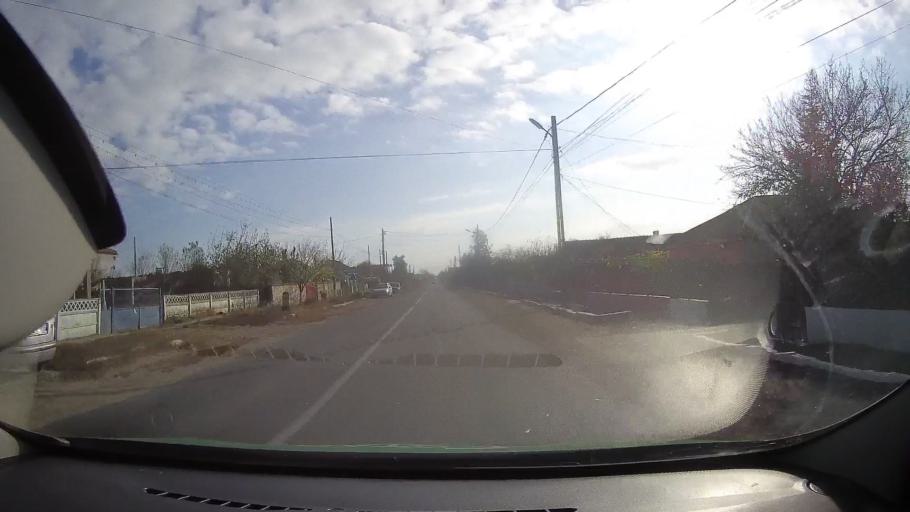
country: RO
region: Constanta
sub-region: Comuna Corbu
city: Corbu
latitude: 44.4051
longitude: 28.6615
